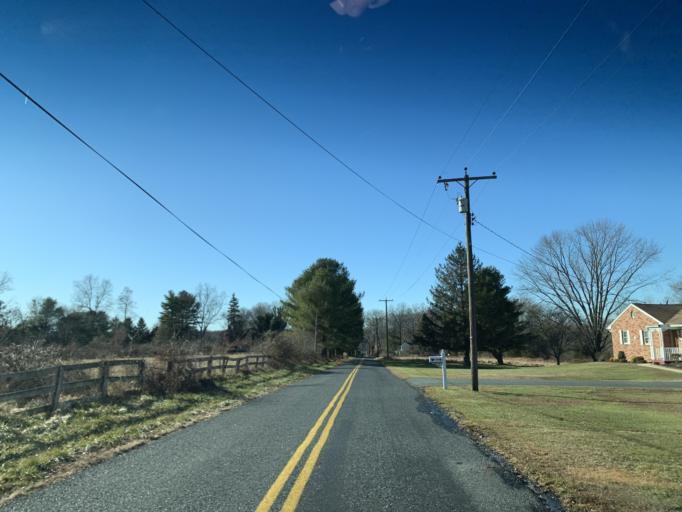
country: US
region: Maryland
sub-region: Harford County
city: Riverside
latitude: 39.5351
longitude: -76.2495
